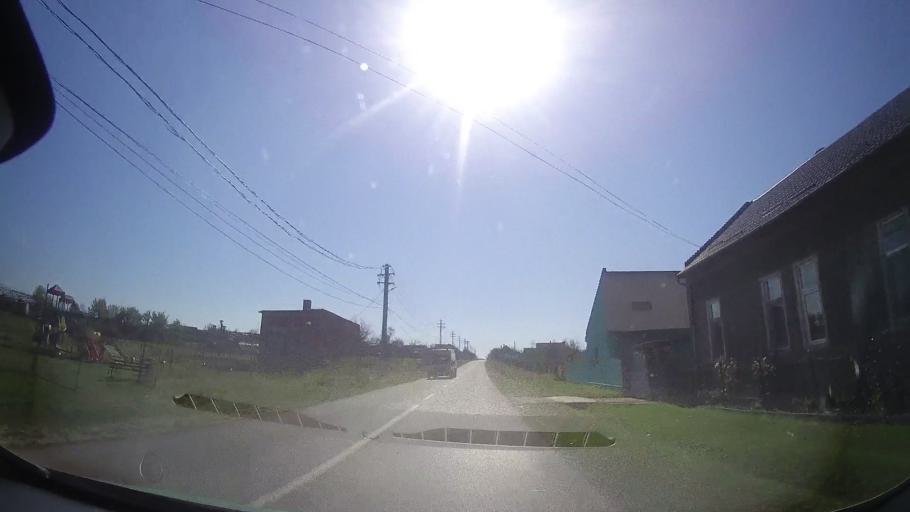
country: RO
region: Timis
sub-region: Comuna Bethausen
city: Bethausen
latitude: 45.7975
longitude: 21.9643
